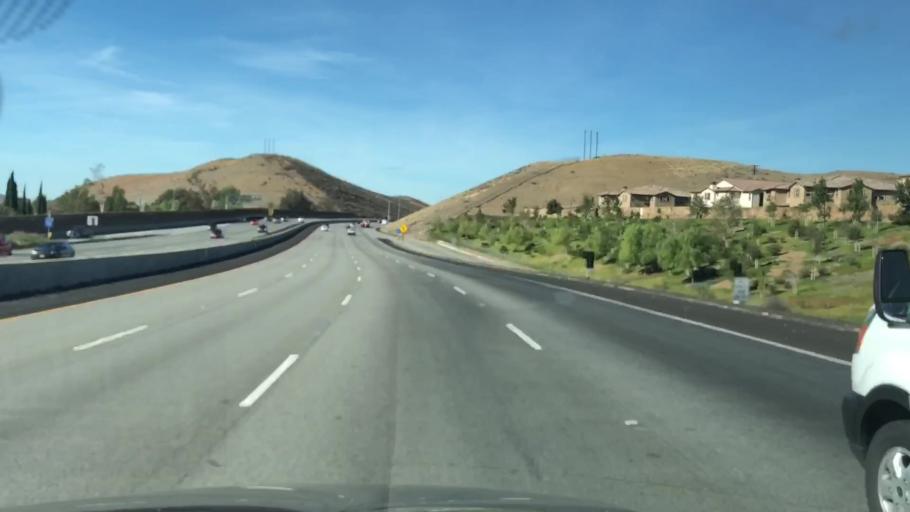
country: US
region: California
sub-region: Ventura County
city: Santa Susana
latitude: 34.2792
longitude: -118.6628
